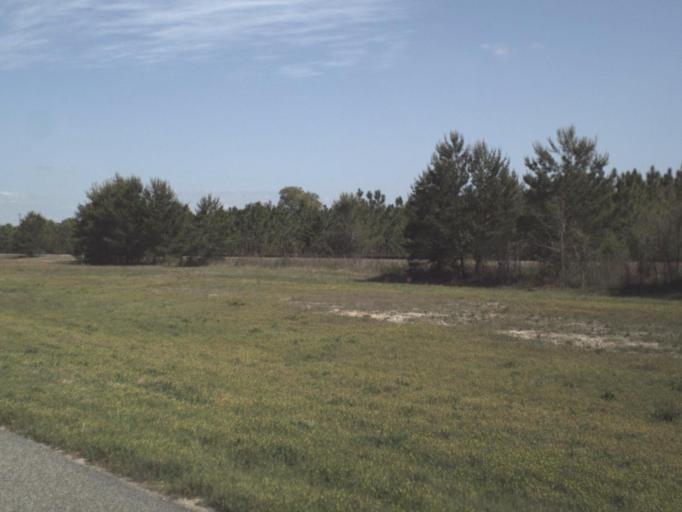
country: US
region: Florida
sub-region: Okaloosa County
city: Crestview
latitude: 30.7515
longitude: -86.4403
